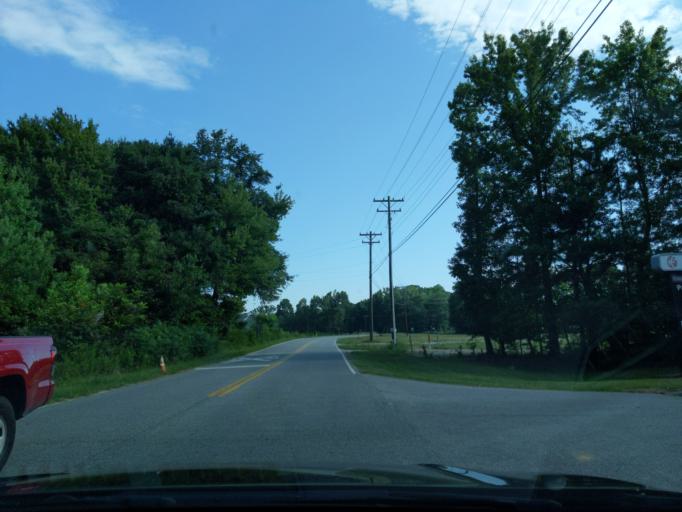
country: US
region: South Carolina
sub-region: Greenville County
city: Mauldin
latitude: 34.8061
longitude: -82.3116
